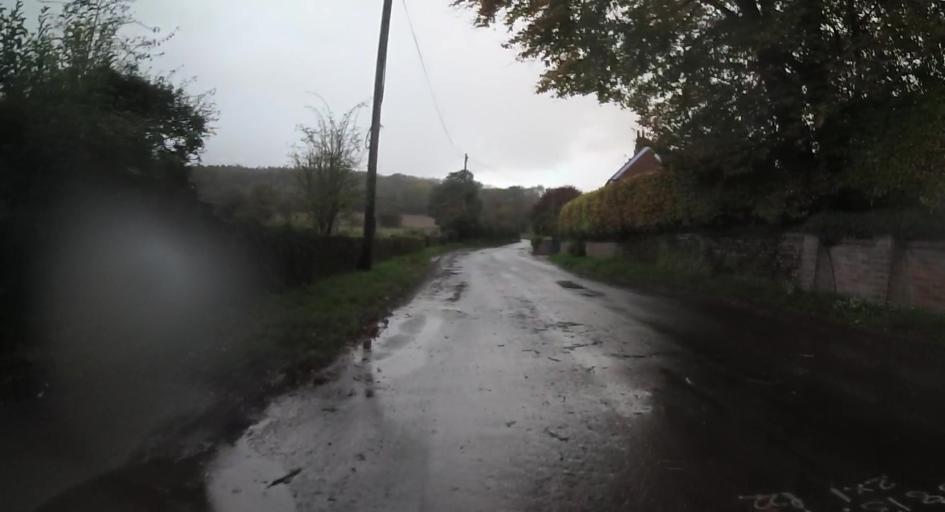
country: GB
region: England
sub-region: Hampshire
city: Long Sutton
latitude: 51.1950
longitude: -0.9181
